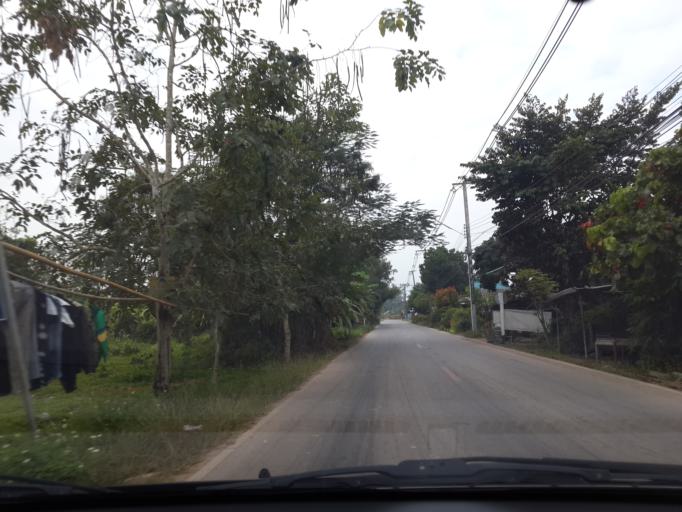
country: TH
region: Chiang Mai
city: San Sai
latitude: 18.8869
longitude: 99.0851
